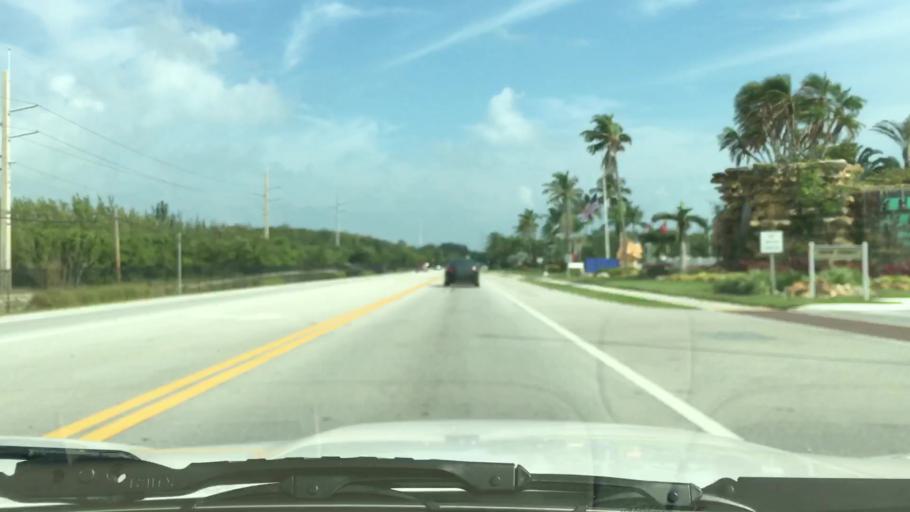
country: US
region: Florida
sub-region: Monroe County
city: Islamorada
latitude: 24.9443
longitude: -80.6048
